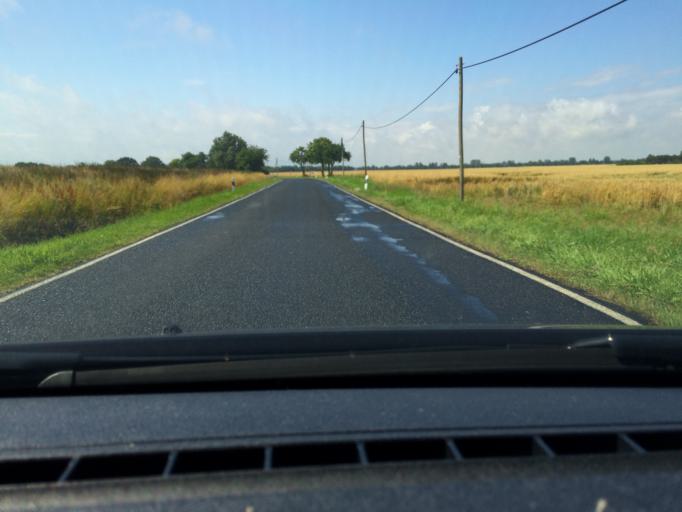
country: DE
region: Mecklenburg-Vorpommern
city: Niepars
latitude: 54.3406
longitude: 12.8864
